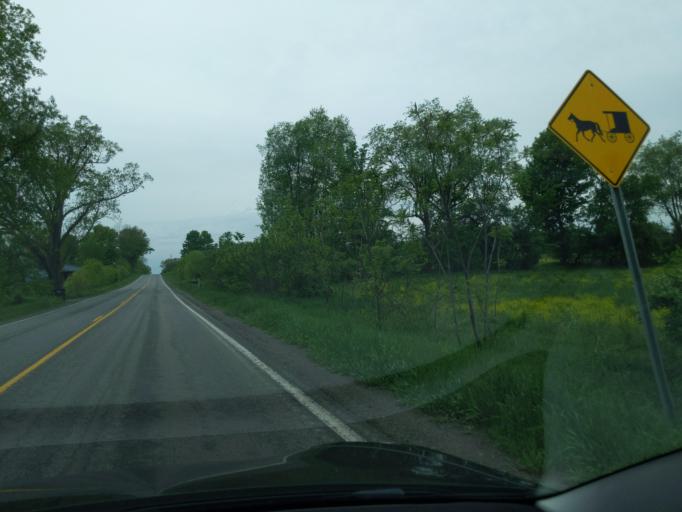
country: US
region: Michigan
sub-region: Ingham County
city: Leslie
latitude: 42.4475
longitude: -84.3834
